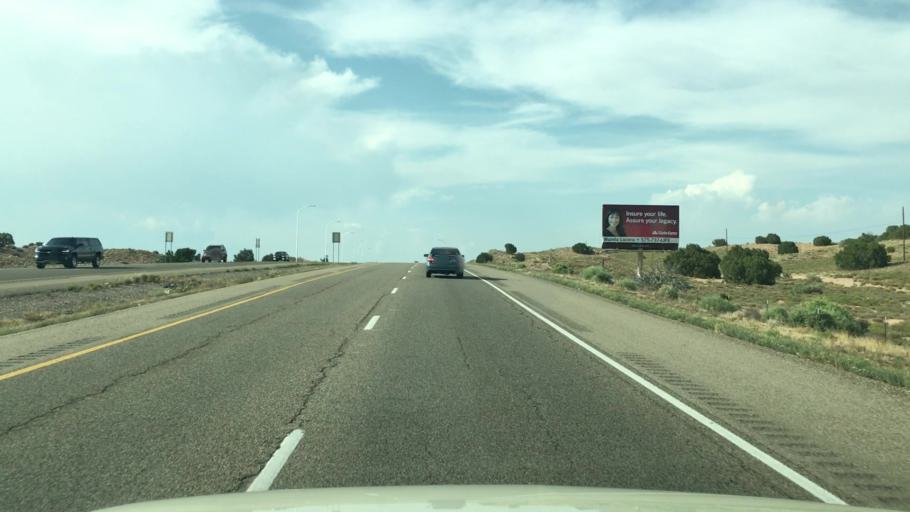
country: US
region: New Mexico
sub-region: Santa Fe County
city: Pojoaque
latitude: 35.9207
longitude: -106.0167
